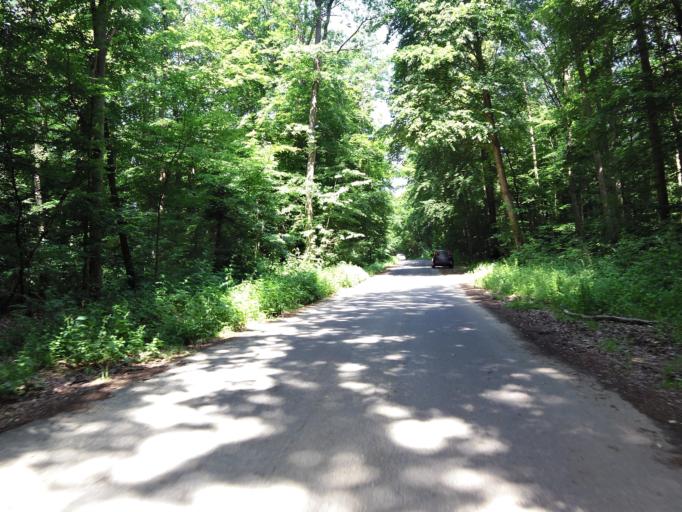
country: DE
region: Bavaria
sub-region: Regierungsbezirk Unterfranken
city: Kist
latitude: 49.7586
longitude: 9.8548
